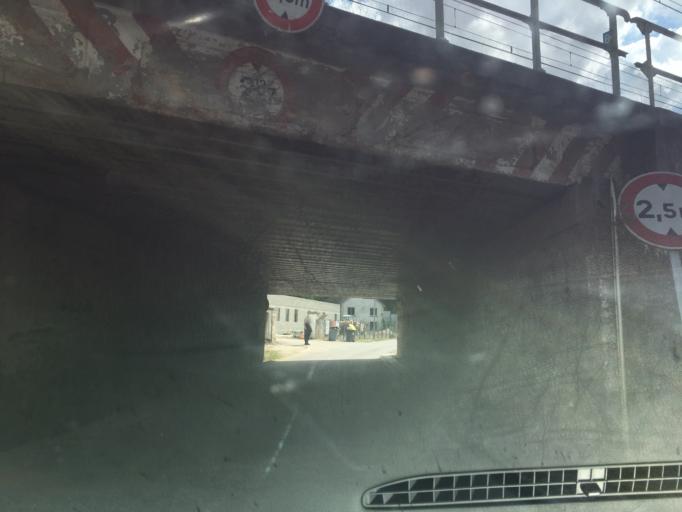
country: FR
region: Bourgogne
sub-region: Departement de l'Yonne
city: Joigny
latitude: 47.9728
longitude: 3.3844
